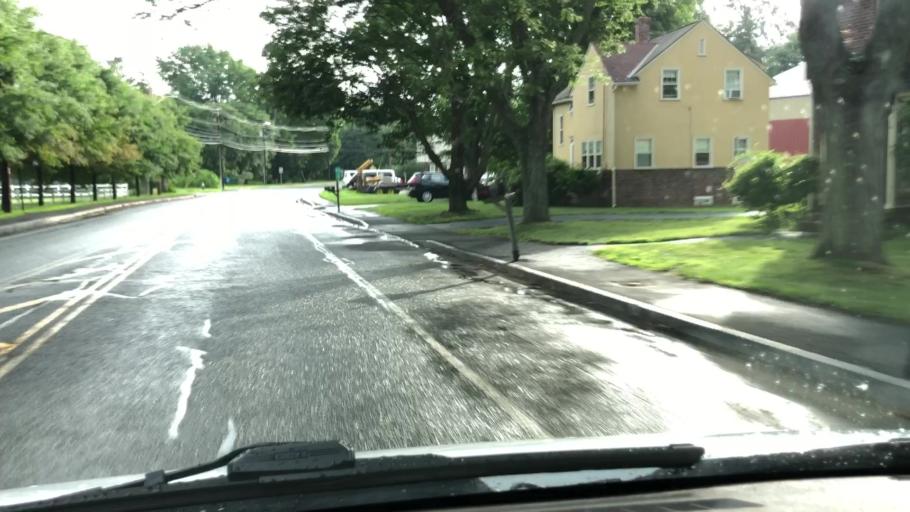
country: US
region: Massachusetts
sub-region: Hampshire County
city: Northampton
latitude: 42.3118
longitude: -72.6428
